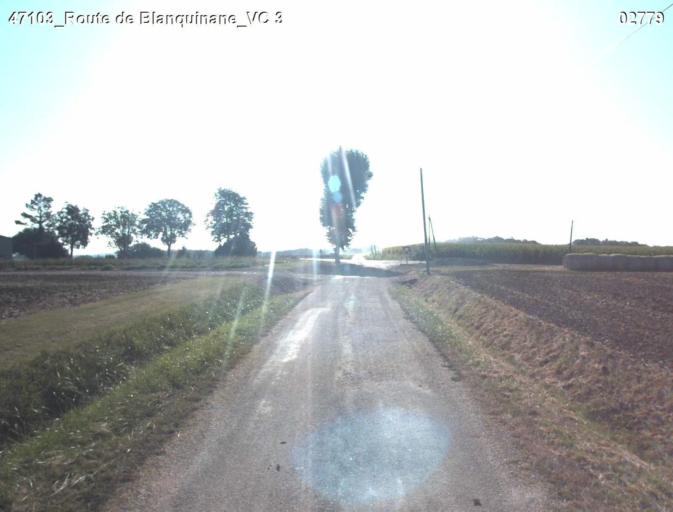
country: FR
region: Aquitaine
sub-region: Departement du Lot-et-Garonne
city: Nerac
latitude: 44.0893
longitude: 0.3331
